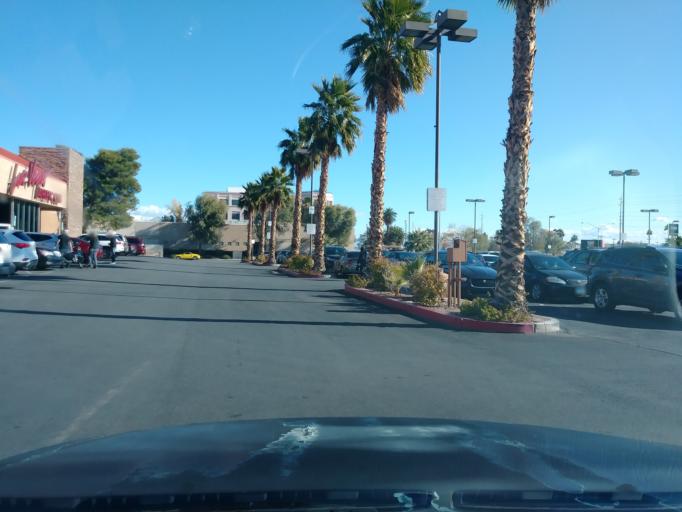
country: US
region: Nevada
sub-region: Clark County
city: Spring Valley
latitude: 36.1454
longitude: -115.2134
